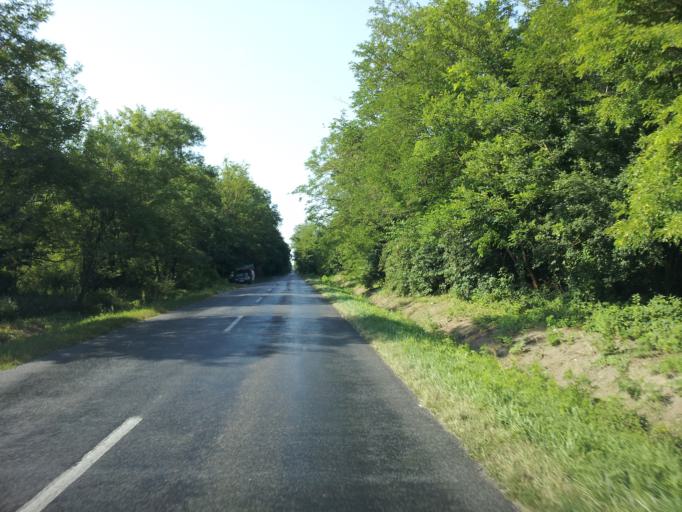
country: HU
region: Zala
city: Cserszegtomaj
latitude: 46.8512
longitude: 17.1980
